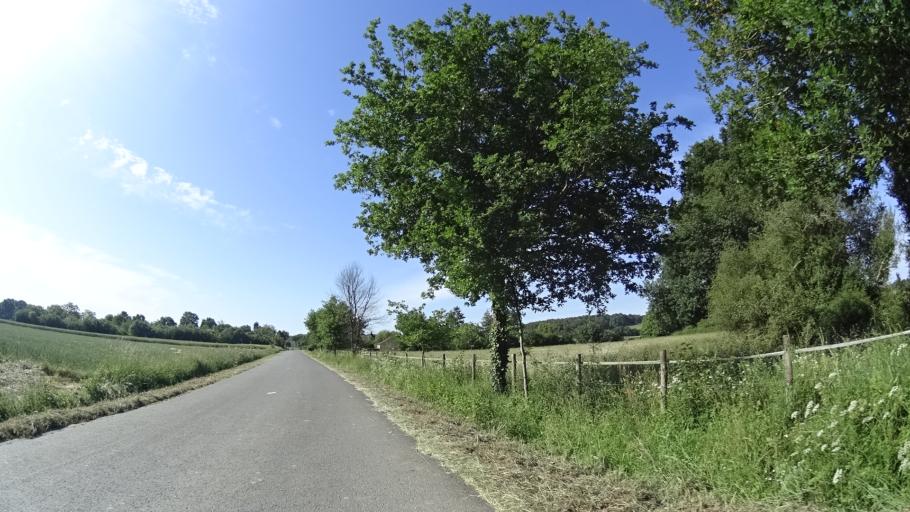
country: FR
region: Brittany
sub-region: Departement d'Ille-et-Vilaine
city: Guipry
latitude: 47.8009
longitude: -1.8489
